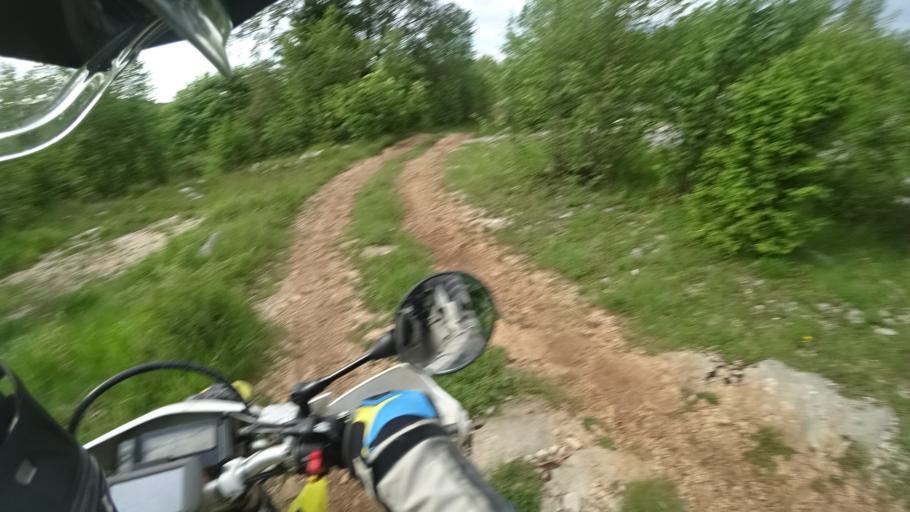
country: HR
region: Sibensko-Kniniska
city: Drnis
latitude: 43.8640
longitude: 16.3923
